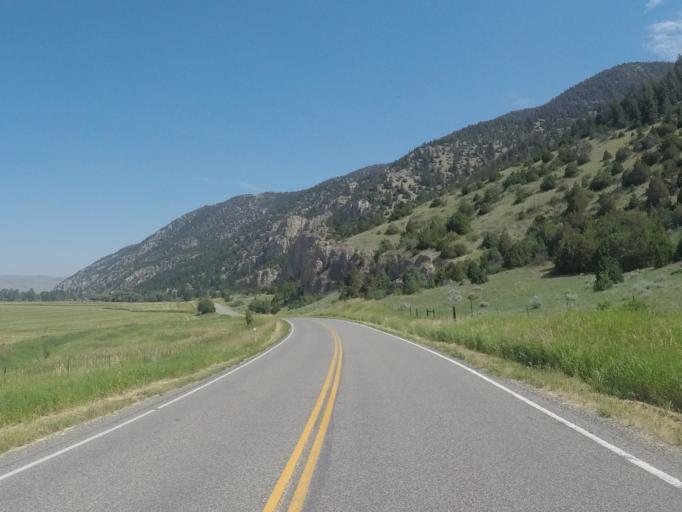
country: US
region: Montana
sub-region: Park County
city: Livingston
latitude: 45.5866
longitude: -110.5608
